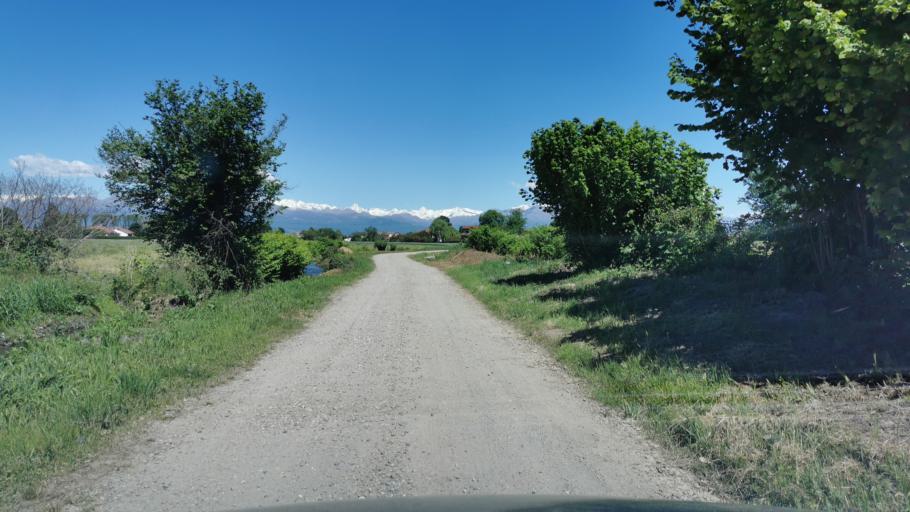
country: IT
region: Piedmont
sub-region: Provincia di Torino
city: Leini
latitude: 45.1668
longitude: 7.7262
